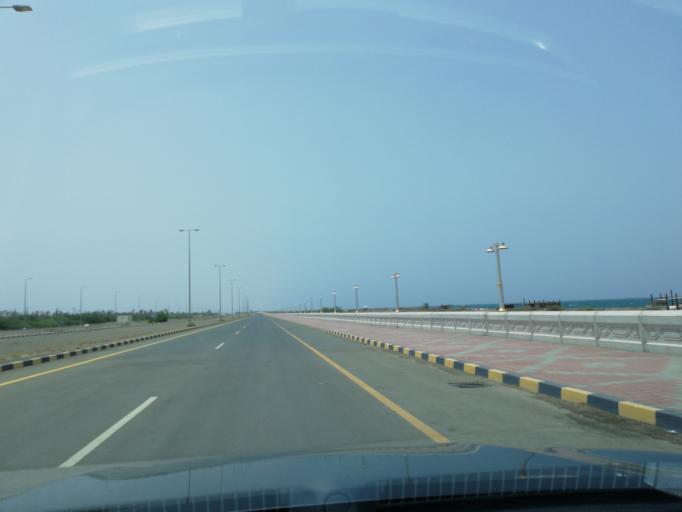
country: OM
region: Al Batinah
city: Al Liwa'
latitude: 24.6225
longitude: 56.5326
